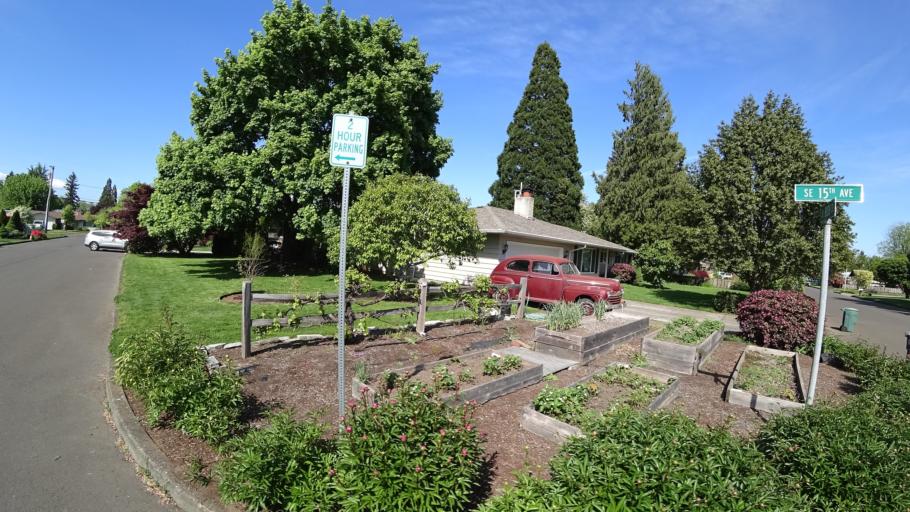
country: US
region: Oregon
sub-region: Washington County
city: Hillsboro
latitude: 45.5106
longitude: -122.9675
